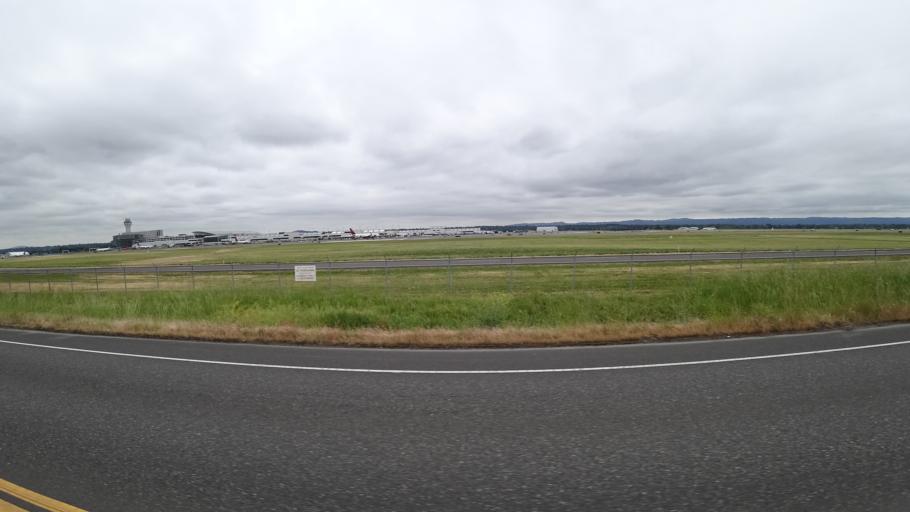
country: US
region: Washington
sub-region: Clark County
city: Walnut Grove
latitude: 45.5968
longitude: -122.5948
